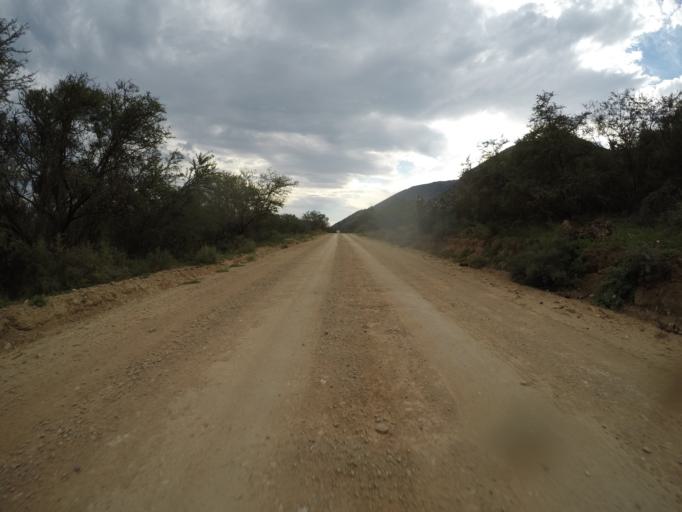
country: ZA
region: Eastern Cape
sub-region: Cacadu District Municipality
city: Kareedouw
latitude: -33.5730
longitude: 24.1312
